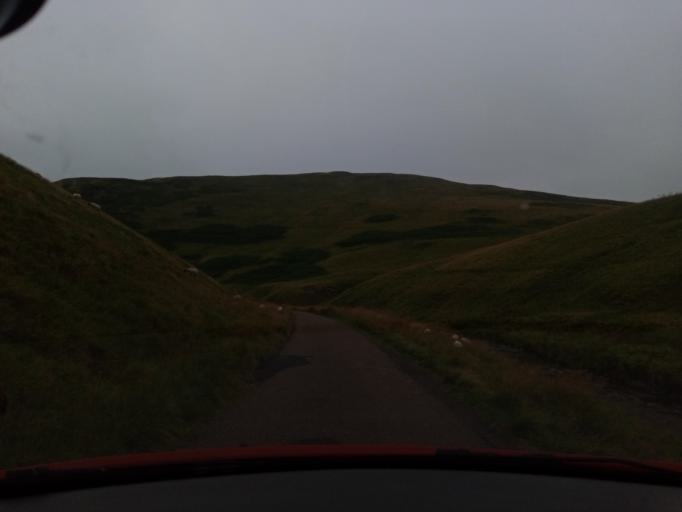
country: GB
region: England
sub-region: Northumberland
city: Rochester
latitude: 55.3913
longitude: -2.2327
